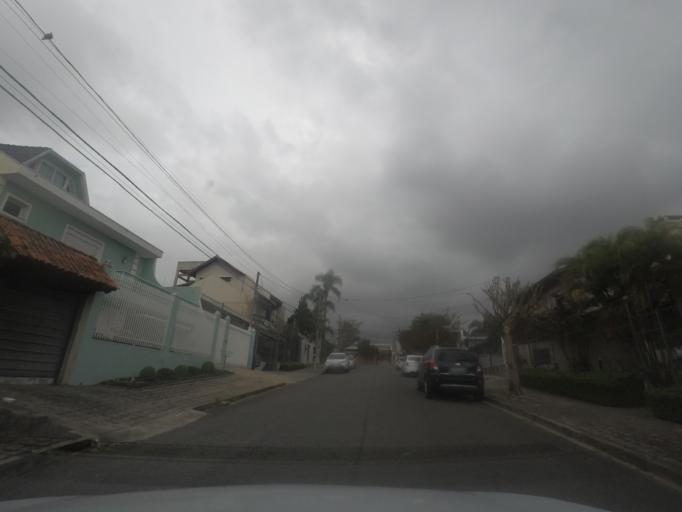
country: BR
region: Parana
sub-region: Curitiba
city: Curitiba
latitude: -25.4412
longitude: -49.2452
